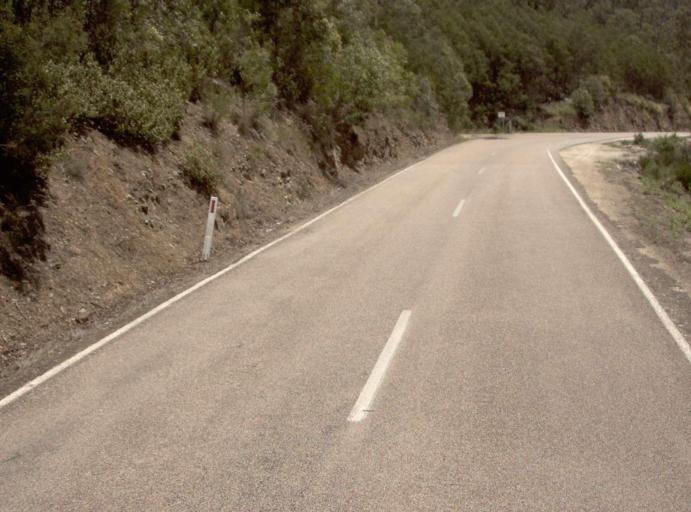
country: AU
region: Victoria
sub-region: East Gippsland
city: Lakes Entrance
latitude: -37.5347
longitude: 147.8553
